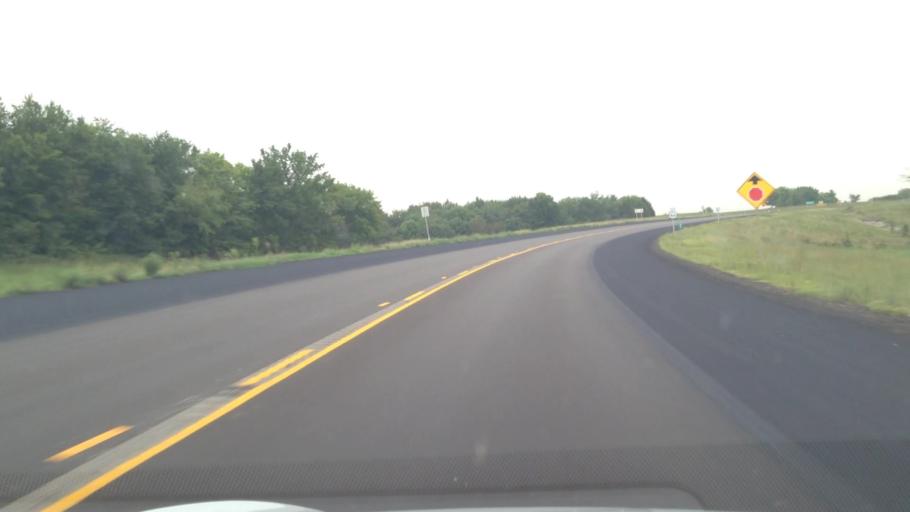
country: US
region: Kansas
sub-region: Cherokee County
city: Baxter Springs
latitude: 37.0275
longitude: -94.7026
